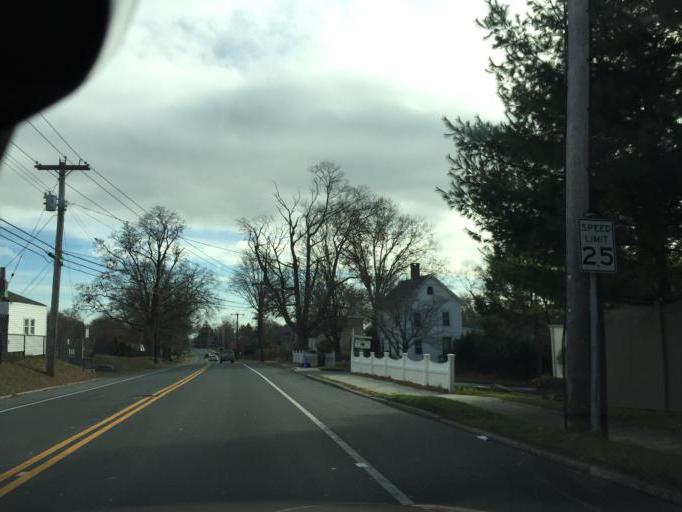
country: US
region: Connecticut
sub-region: Fairfield County
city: Bridgeport
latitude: 41.1768
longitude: -73.2411
